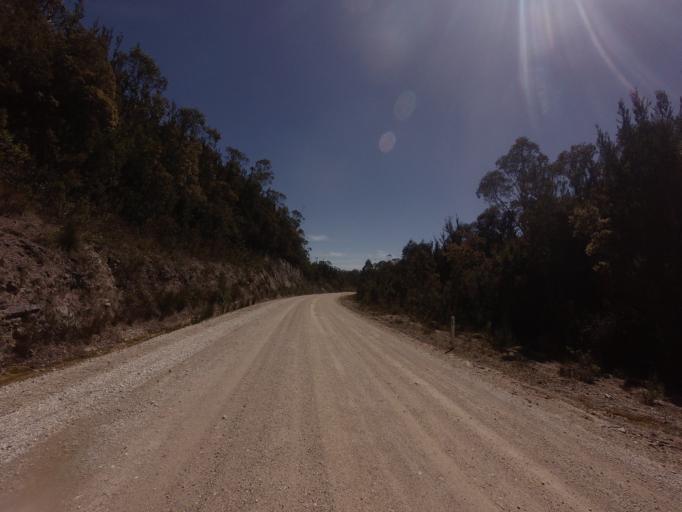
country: AU
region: Tasmania
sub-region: Huon Valley
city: Geeveston
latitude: -42.8170
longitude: 146.3865
